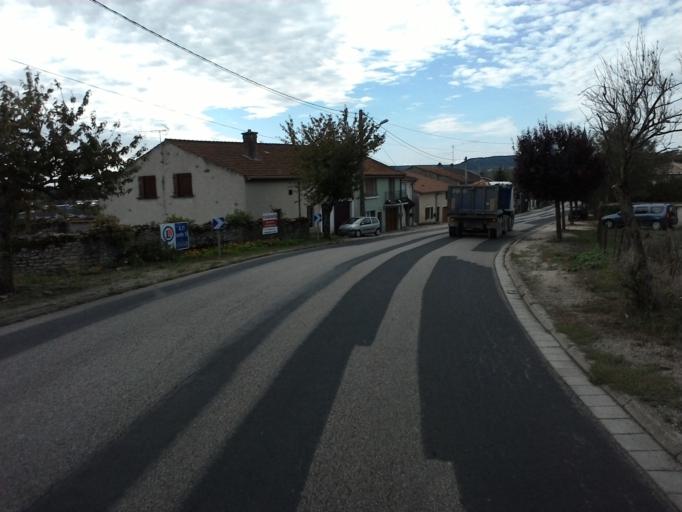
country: FR
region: Lorraine
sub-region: Departement de Meurthe-et-Moselle
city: Ecrouves
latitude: 48.7682
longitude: 5.8657
